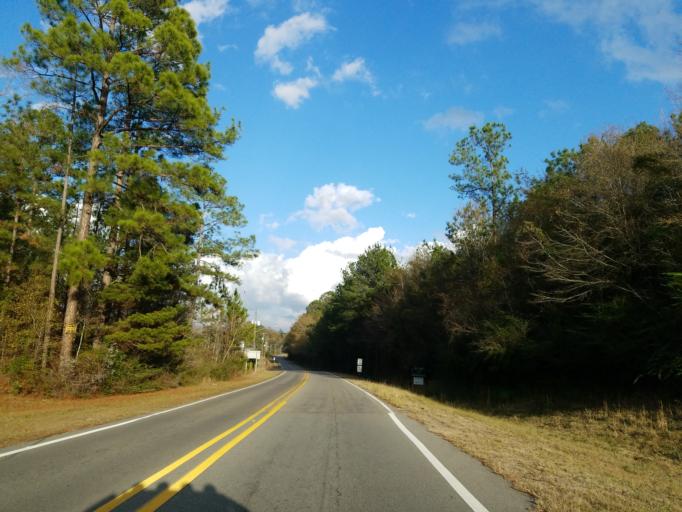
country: US
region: Mississippi
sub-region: Jones County
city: Sharon
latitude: 31.7852
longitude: -89.0541
